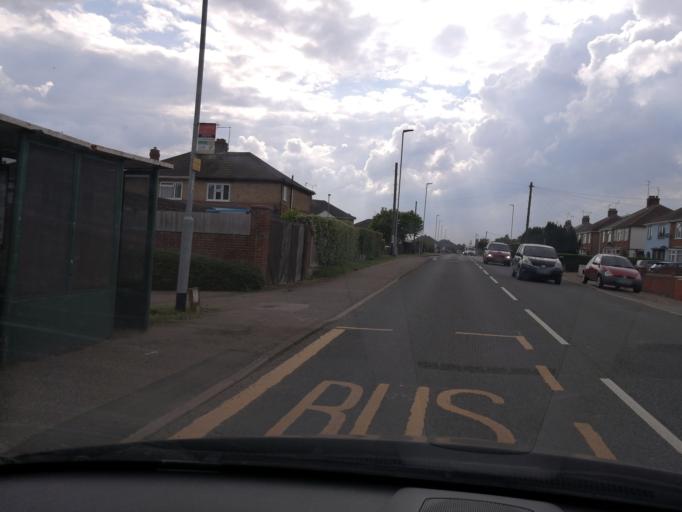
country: GB
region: England
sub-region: Peterborough
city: Peterborough
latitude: 52.5505
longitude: -0.2160
